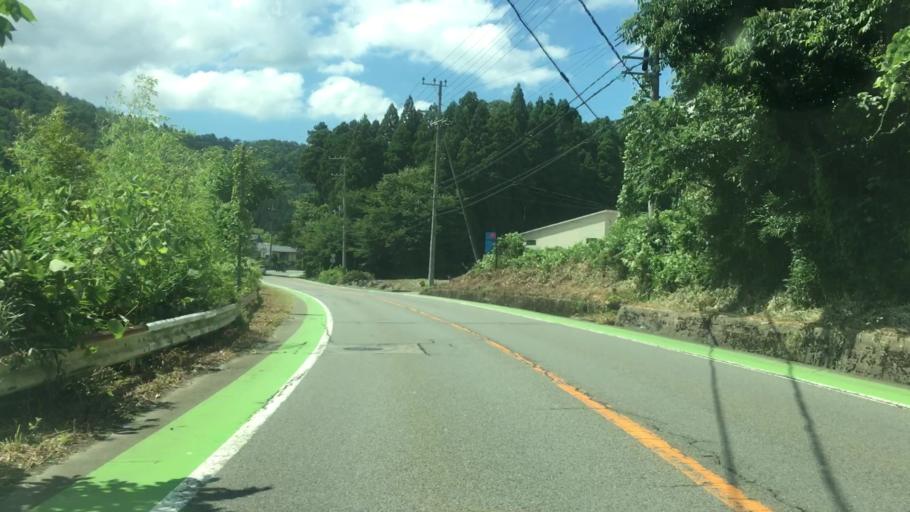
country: JP
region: Hyogo
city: Toyooka
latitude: 35.4761
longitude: 134.7114
